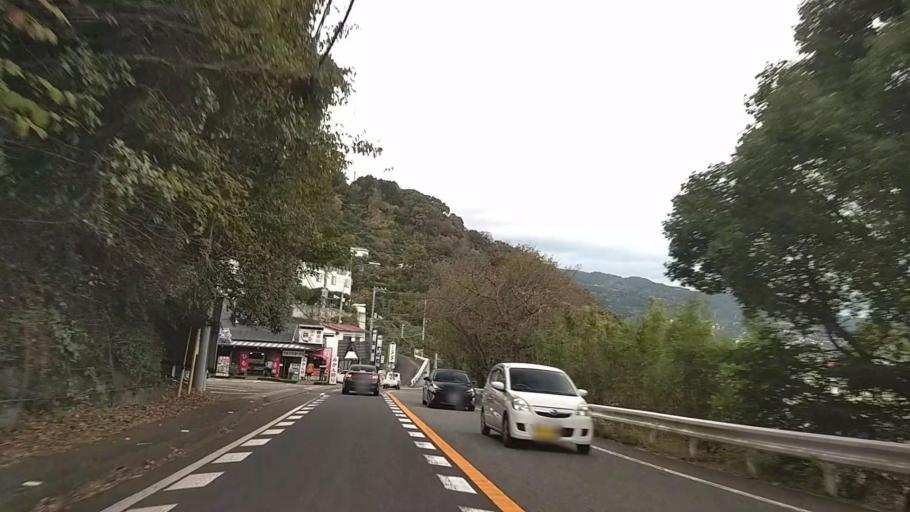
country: JP
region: Kanagawa
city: Yugawara
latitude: 35.1360
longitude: 139.1092
